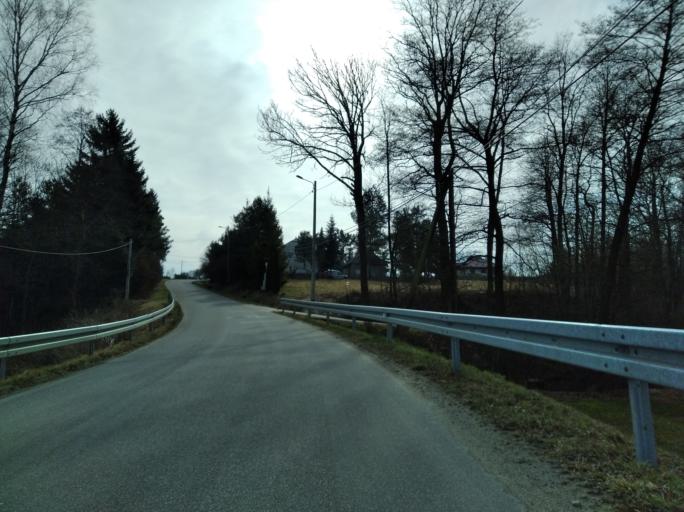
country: PL
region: Subcarpathian Voivodeship
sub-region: Powiat brzozowski
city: Orzechowka
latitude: 49.7390
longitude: 21.9413
